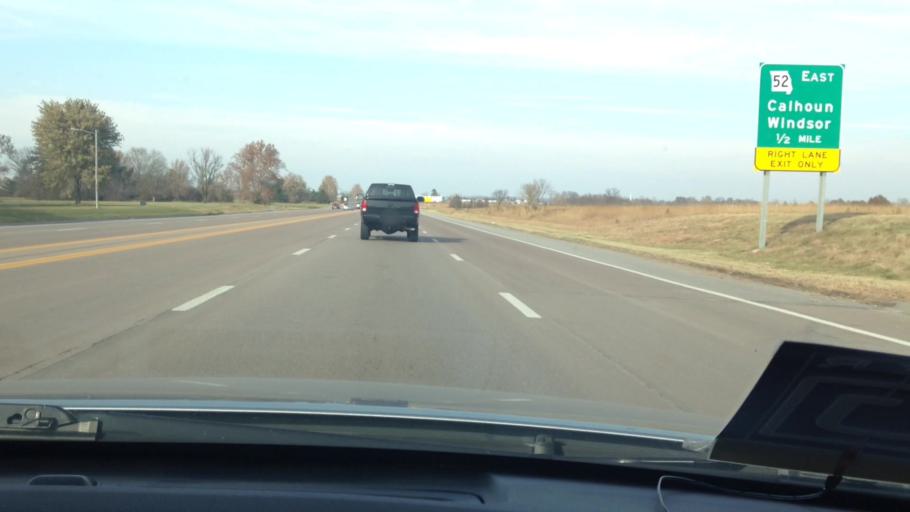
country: US
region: Missouri
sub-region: Henry County
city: Clinton
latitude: 38.3736
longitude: -93.7514
